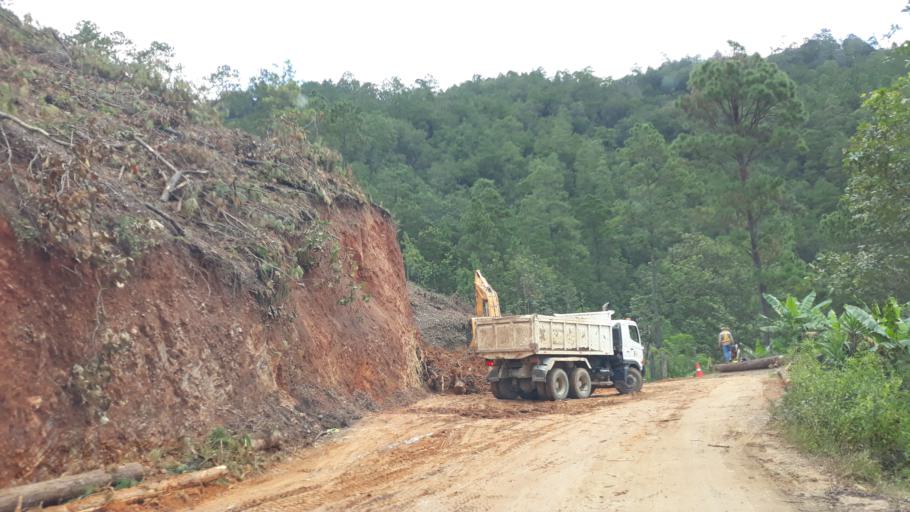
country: HN
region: El Paraiso
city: Santa Cruz
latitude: 13.7568
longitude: -86.6548
